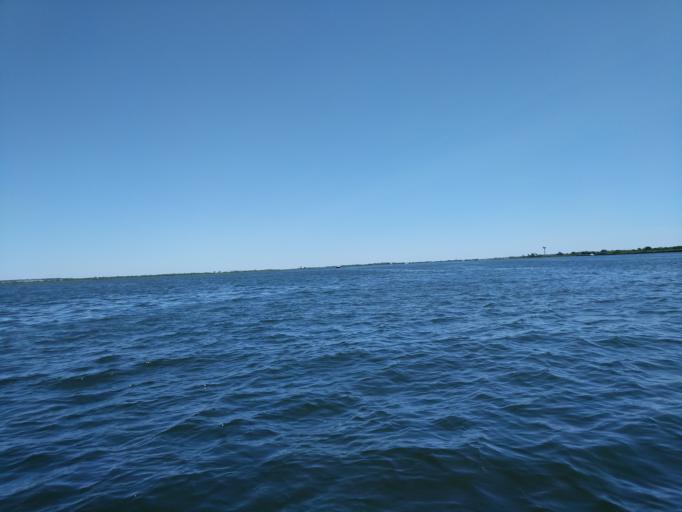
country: US
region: New York
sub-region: Nassau County
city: Lido Beach
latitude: 40.5965
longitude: -73.6270
